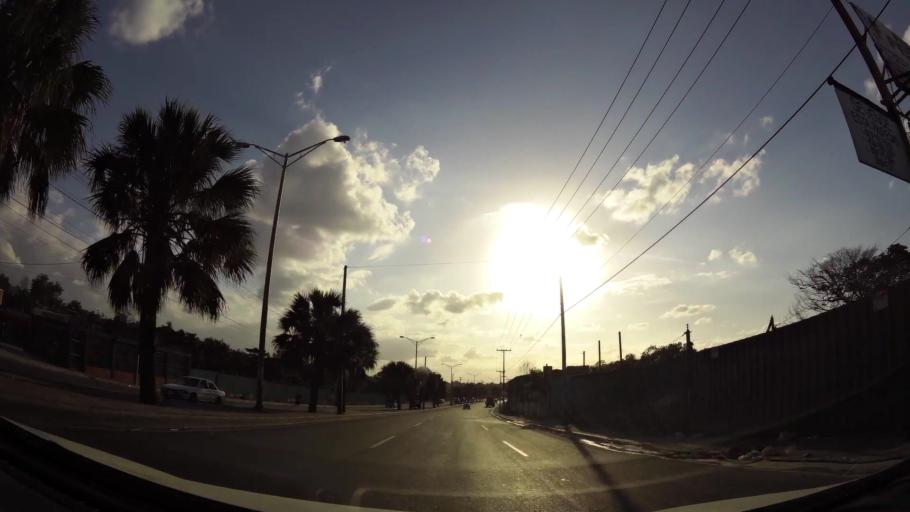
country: DO
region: Nacional
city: Ensanche Luperon
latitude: 18.5467
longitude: -69.9102
